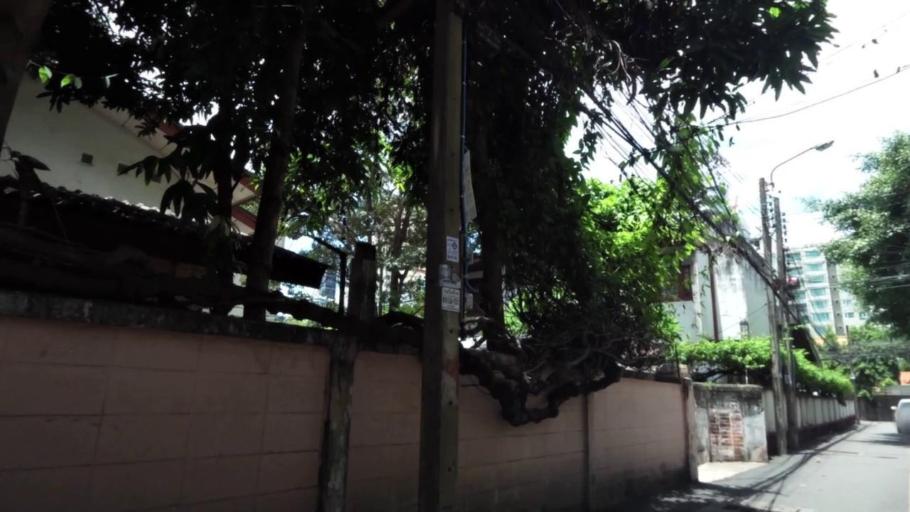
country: TH
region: Bangkok
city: Khlong Toei
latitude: 13.7366
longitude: 100.5658
